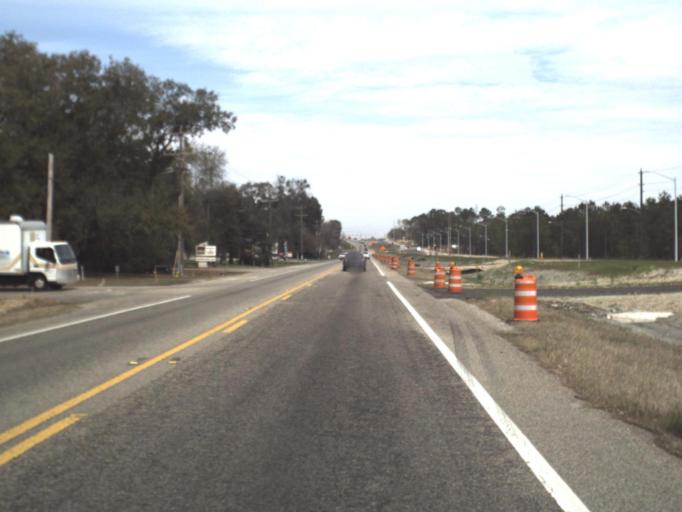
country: US
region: Florida
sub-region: Leon County
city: Tallahassee
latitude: 30.4248
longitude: -84.3528
